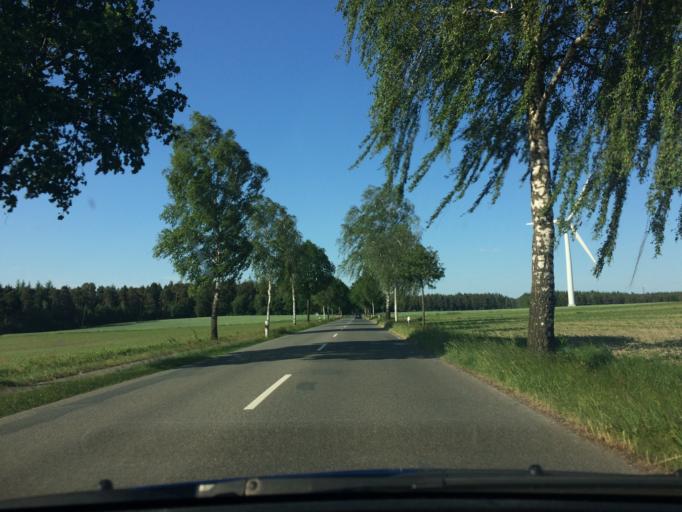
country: DE
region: Lower Saxony
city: Bispingen
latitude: 53.0418
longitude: 9.9332
